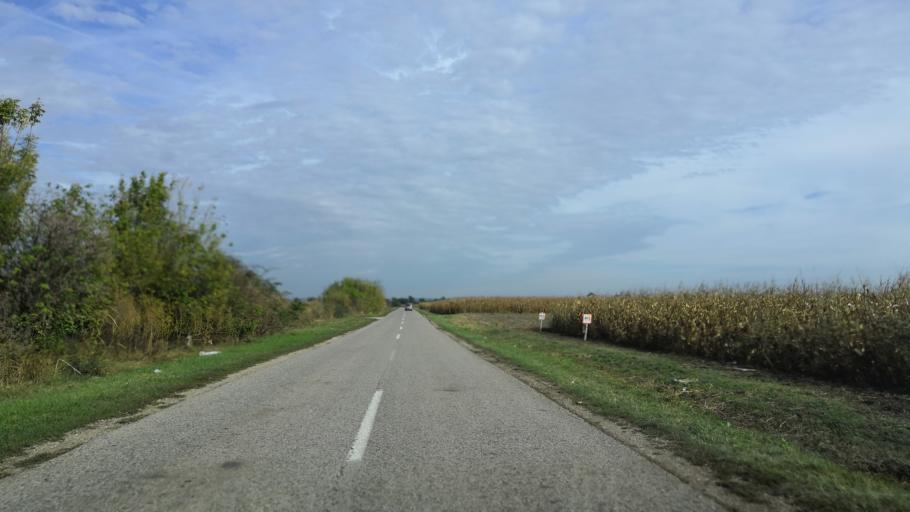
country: RS
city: Novi Karlovci
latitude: 45.0587
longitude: 20.1790
